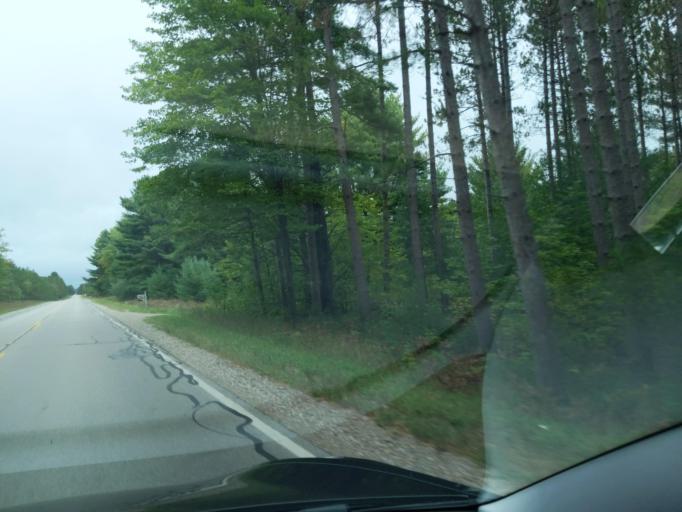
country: US
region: Michigan
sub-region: Grand Traverse County
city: Kingsley
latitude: 44.6235
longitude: -85.3532
